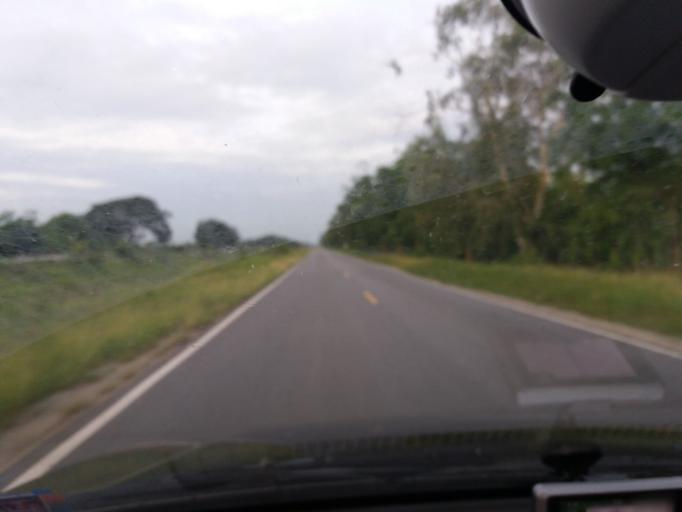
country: TH
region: Suphan Buri
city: Don Chedi
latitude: 14.5472
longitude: 99.9414
